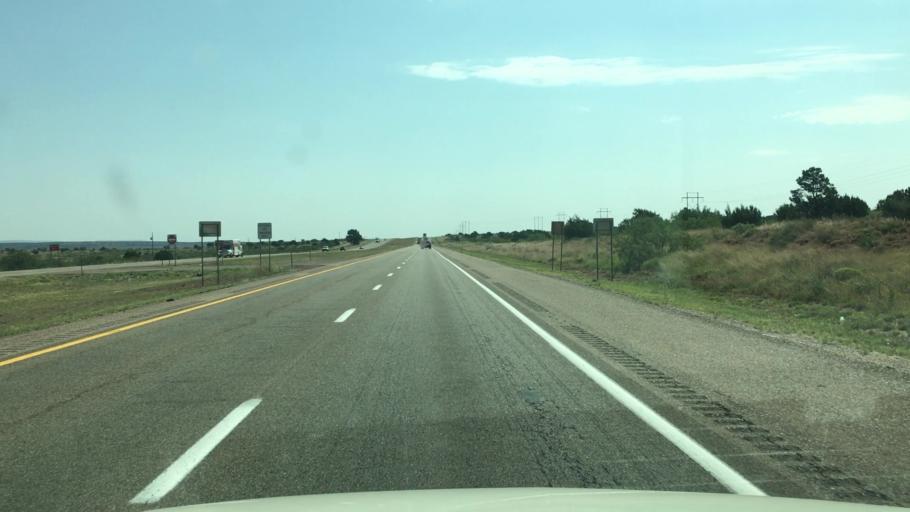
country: US
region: New Mexico
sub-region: Guadalupe County
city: Santa Rosa
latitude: 35.0478
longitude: -104.3726
